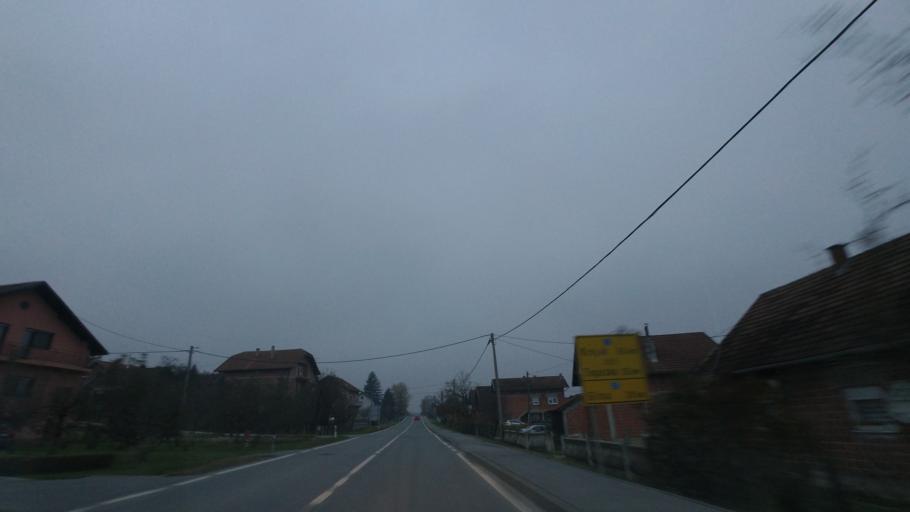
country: HR
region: Sisacko-Moslavacka
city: Petrinja
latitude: 45.4392
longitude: 16.2565
